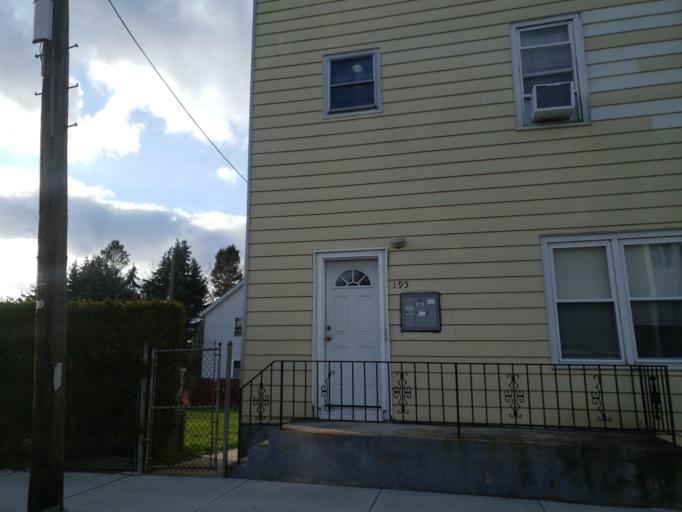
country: US
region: Massachusetts
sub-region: Bristol County
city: Fall River
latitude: 41.6923
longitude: -71.1374
